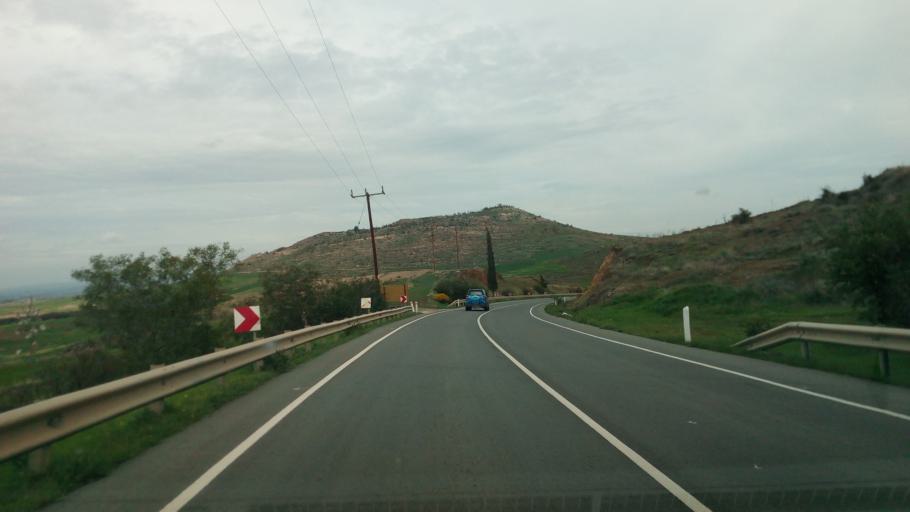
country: CY
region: Lefkosia
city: Lefka
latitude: 35.0829
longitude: 32.9504
